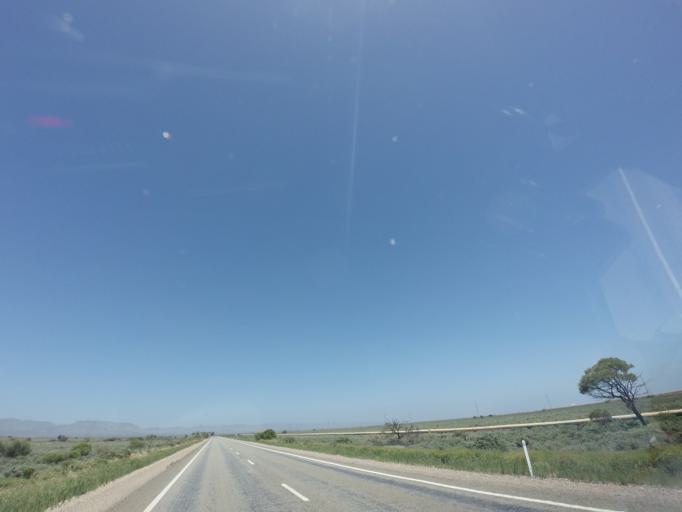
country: AU
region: South Australia
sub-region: Port Augusta
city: Port Augusta
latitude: -32.5358
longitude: 137.8460
